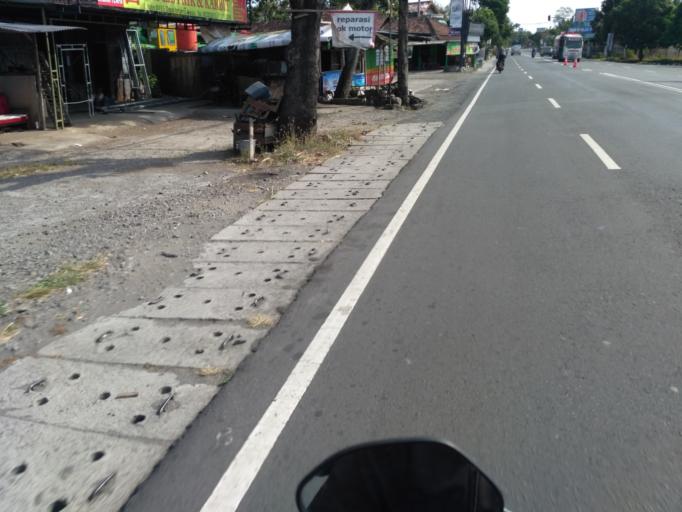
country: ID
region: Daerah Istimewa Yogyakarta
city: Godean
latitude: -7.8105
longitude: 110.2807
